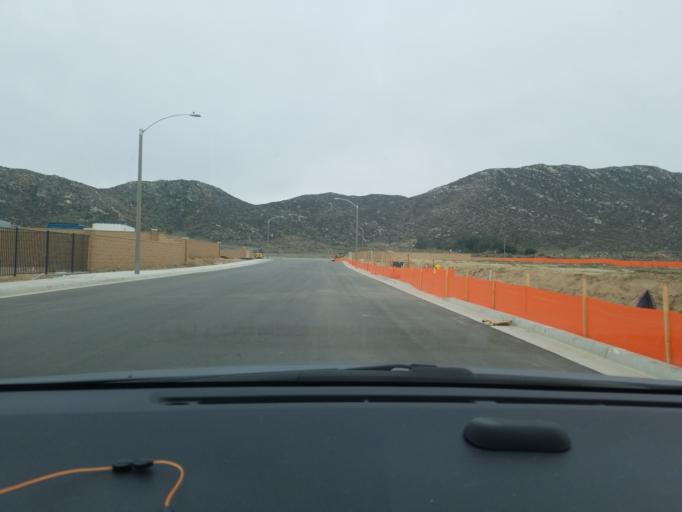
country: US
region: California
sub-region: Riverside County
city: Winchester
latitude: 33.6941
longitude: -117.0980
